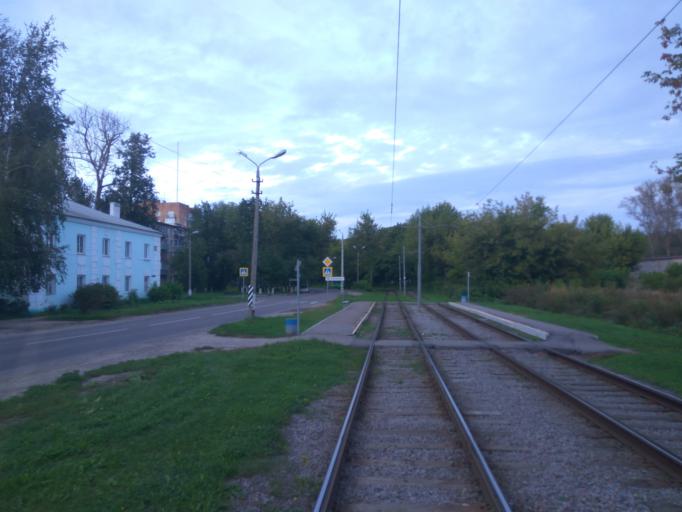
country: RU
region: Moskovskaya
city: Kolomna
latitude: 55.0773
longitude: 38.8159
